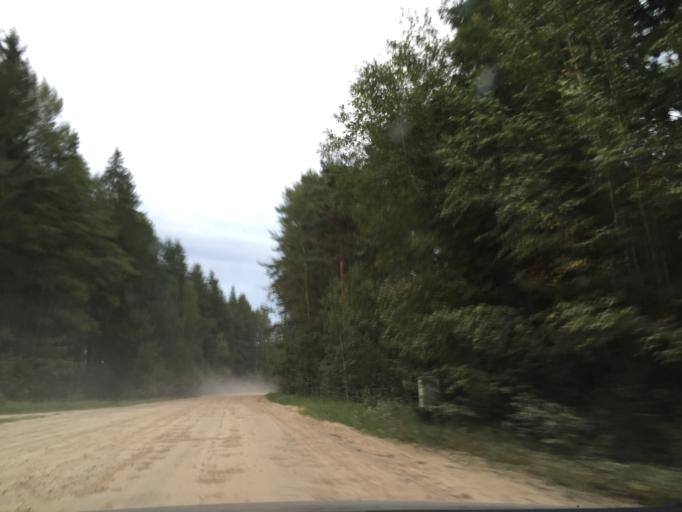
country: LT
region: Panevezys
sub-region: Birzai
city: Birzai
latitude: 56.3807
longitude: 24.6279
